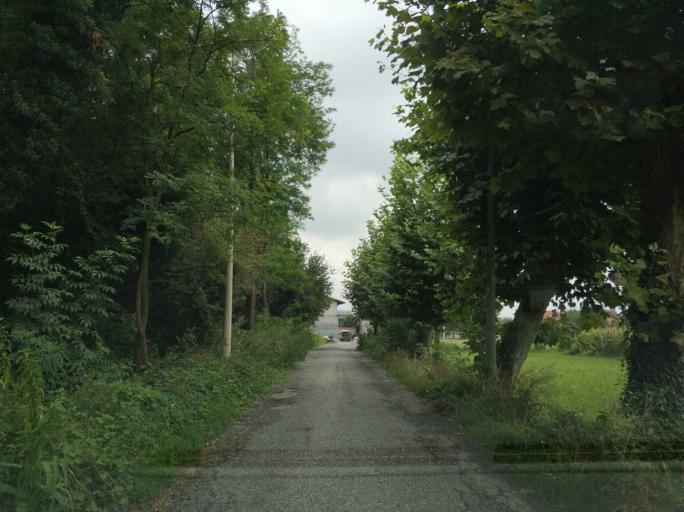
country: IT
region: Piedmont
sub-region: Provincia di Torino
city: Cirie
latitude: 45.2232
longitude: 7.5964
